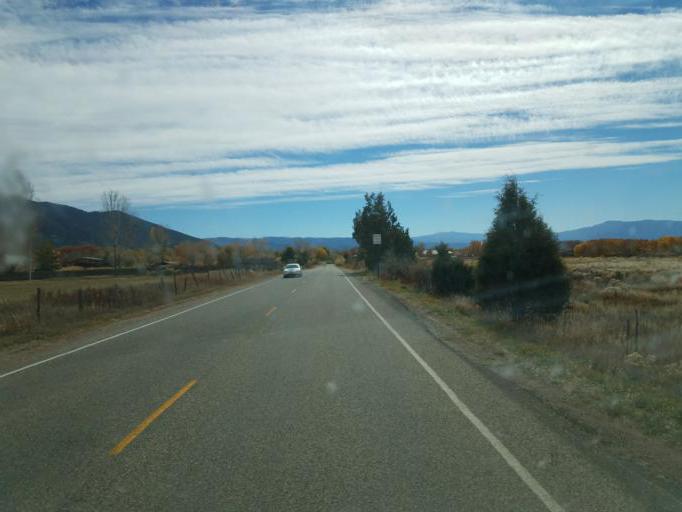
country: US
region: New Mexico
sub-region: Taos County
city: Arroyo Seco
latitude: 36.5223
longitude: -105.5699
